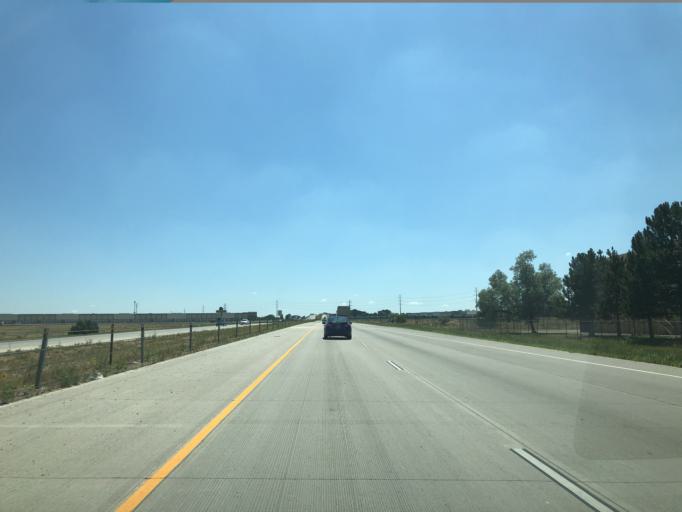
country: US
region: Colorado
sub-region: Adams County
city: Aurora
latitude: 39.7575
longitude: -104.7673
